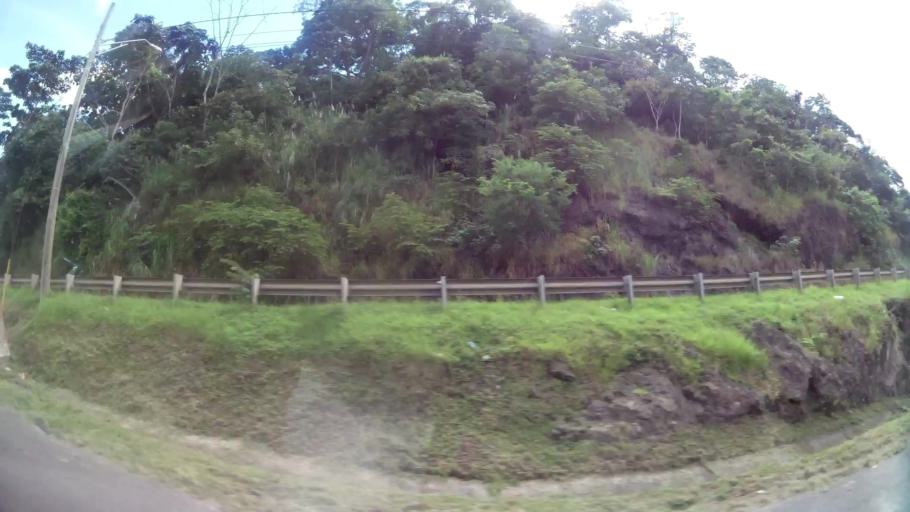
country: PA
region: Panama
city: Las Cumbres
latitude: 9.0400
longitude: -79.5475
